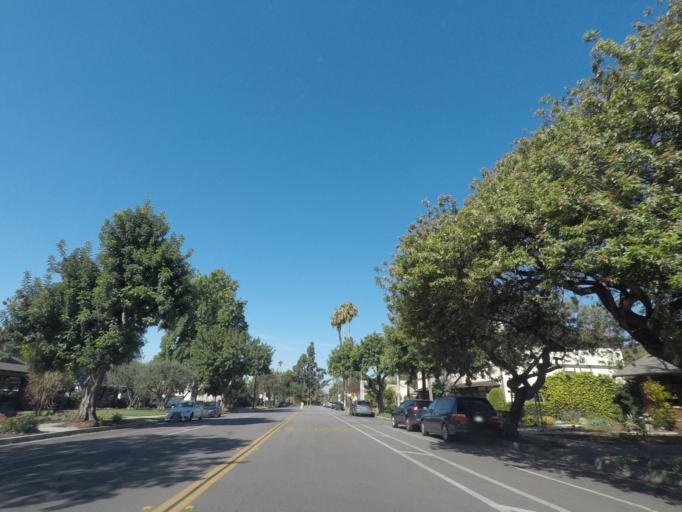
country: US
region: California
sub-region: Los Angeles County
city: South Pasadena
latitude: 34.1141
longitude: -118.1656
